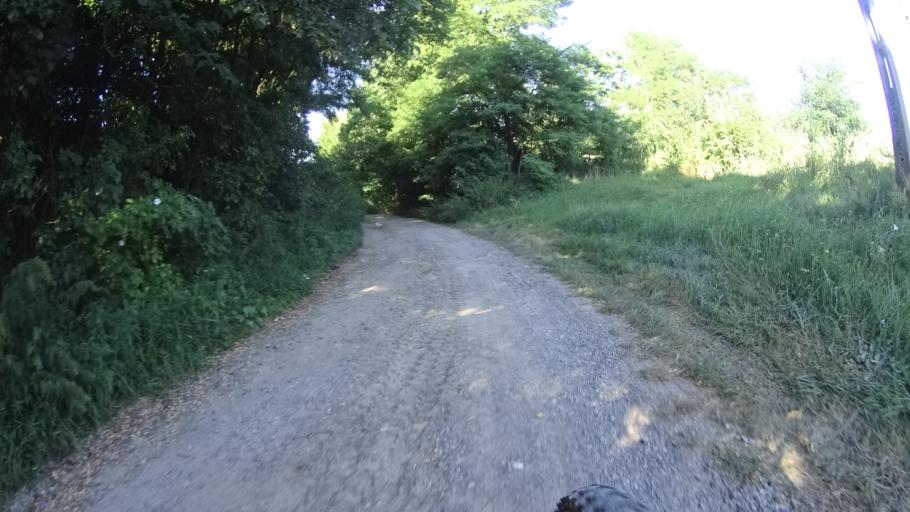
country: PL
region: Masovian Voivodeship
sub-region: Powiat bialobrzeski
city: Wysmierzyce
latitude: 51.6619
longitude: 20.8498
